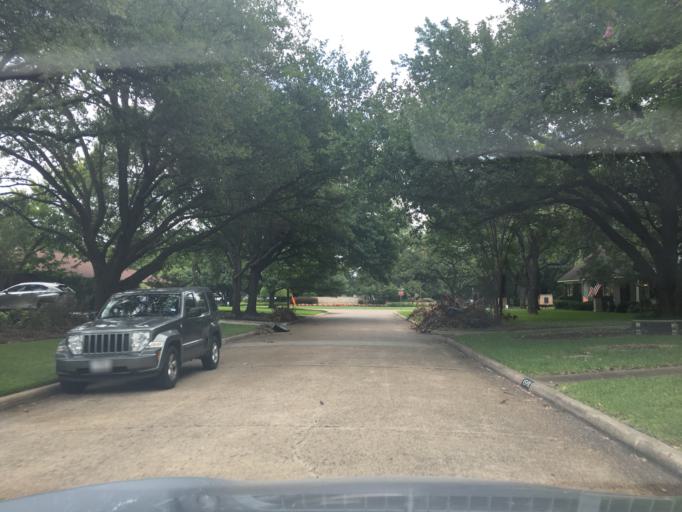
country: US
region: Texas
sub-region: Dallas County
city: Addison
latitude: 32.9071
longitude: -96.8306
